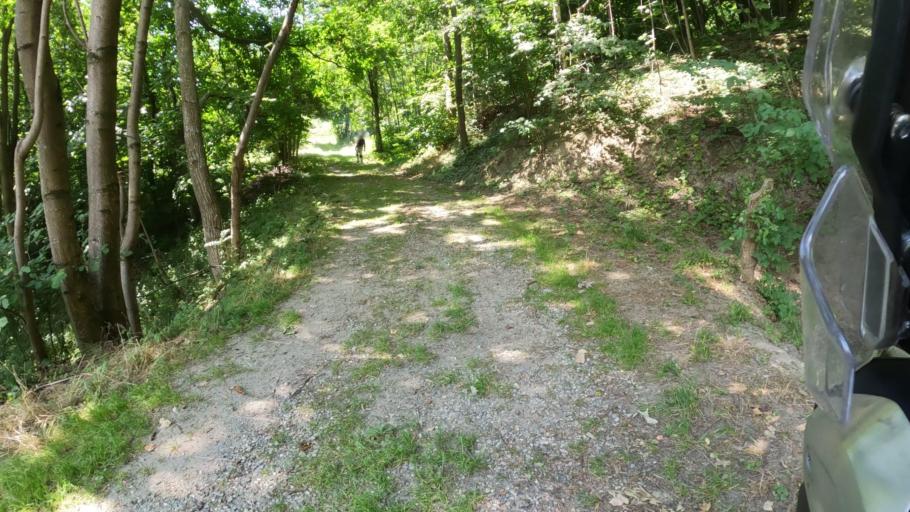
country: IT
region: Piedmont
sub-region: Provincia di Torino
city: Sant'Antonino di Susa
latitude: 45.1413
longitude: 7.2795
